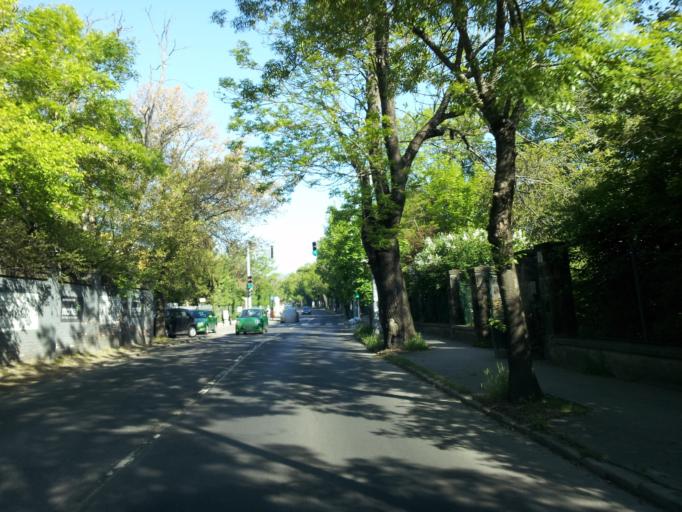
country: HU
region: Budapest
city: Budapest XII. keruelet
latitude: 47.5209
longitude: 18.9987
